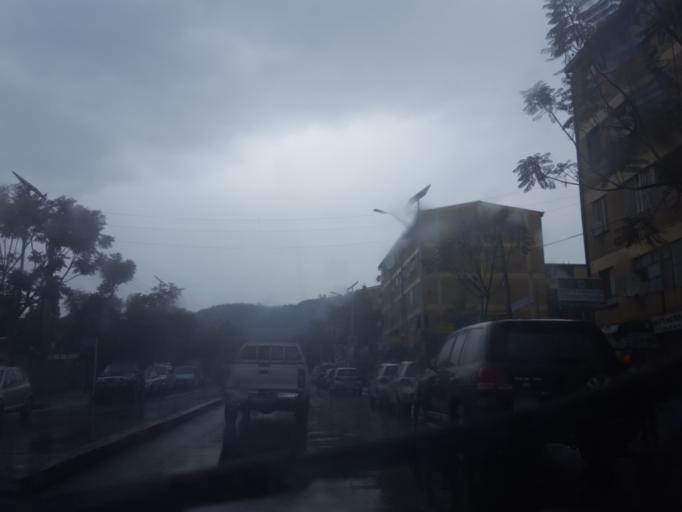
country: ET
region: Adis Abeba
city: Addis Ababa
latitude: 9.0251
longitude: 38.7812
